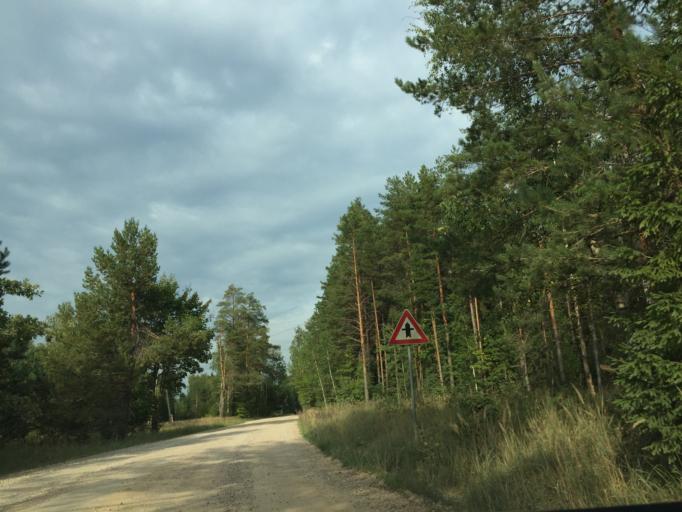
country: LV
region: Ikskile
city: Ikskile
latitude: 56.8065
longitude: 24.4413
